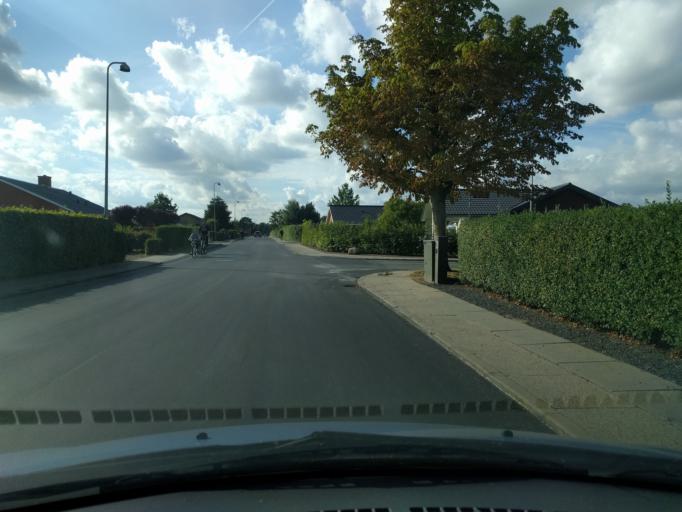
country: DK
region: South Denmark
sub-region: Odense Kommune
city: Neder Holluf
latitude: 55.3562
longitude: 10.5006
